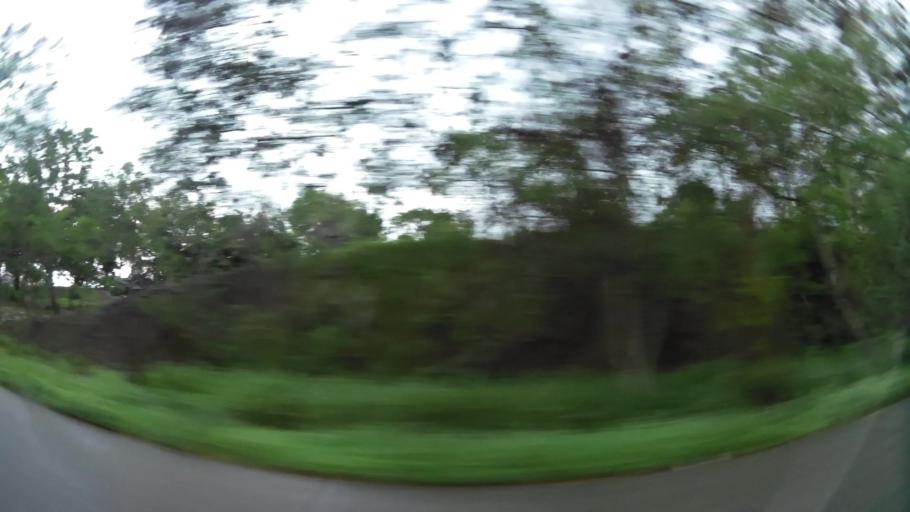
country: DO
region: San Cristobal
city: Villa Altagracia
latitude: 18.6073
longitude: -70.1452
